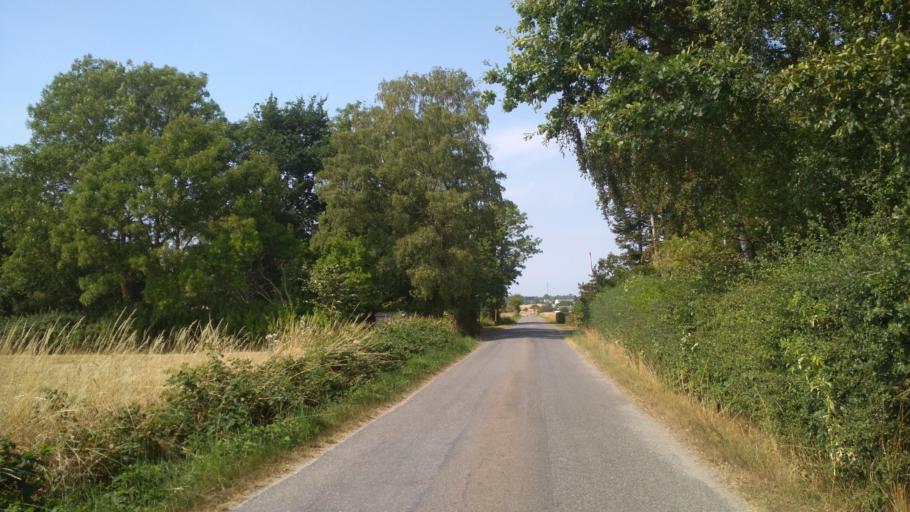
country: DK
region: Capital Region
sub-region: Bornholm Kommune
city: Akirkeby
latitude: 55.0614
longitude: 14.9485
